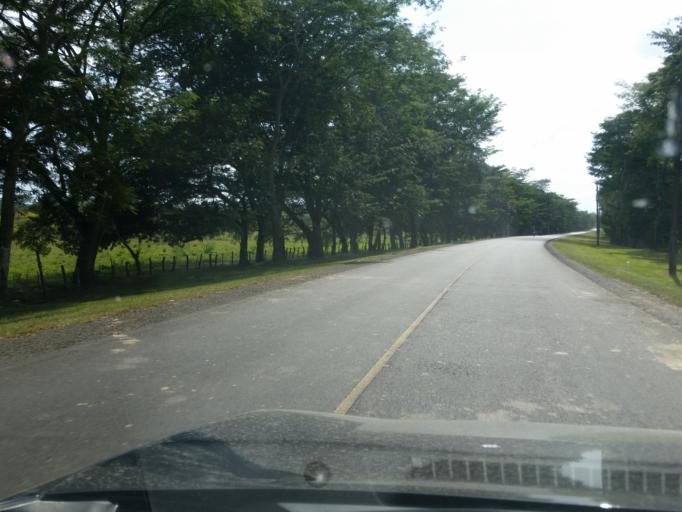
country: NI
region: Rio San Juan
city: San Miguelito
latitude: 11.5257
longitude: -84.8295
